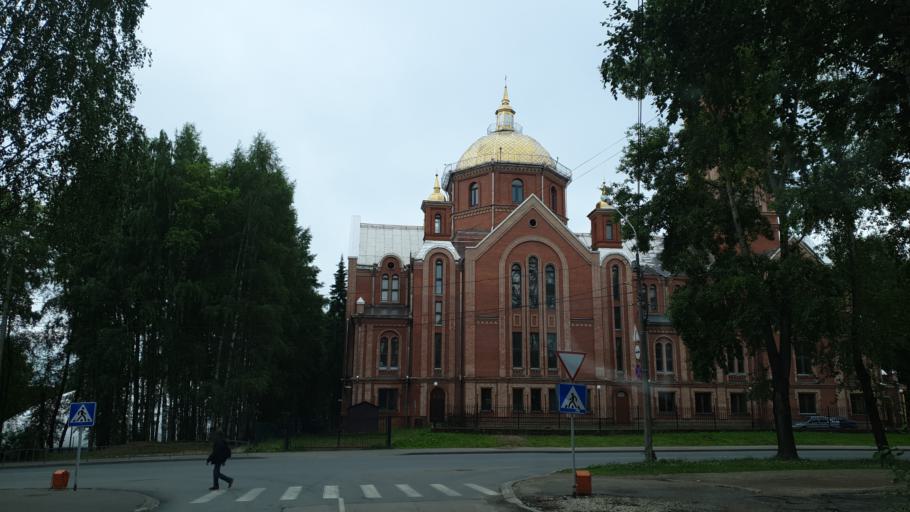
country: RU
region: Komi Republic
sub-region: Syktyvdinskiy Rayon
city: Syktyvkar
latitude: 61.6600
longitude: 50.8230
